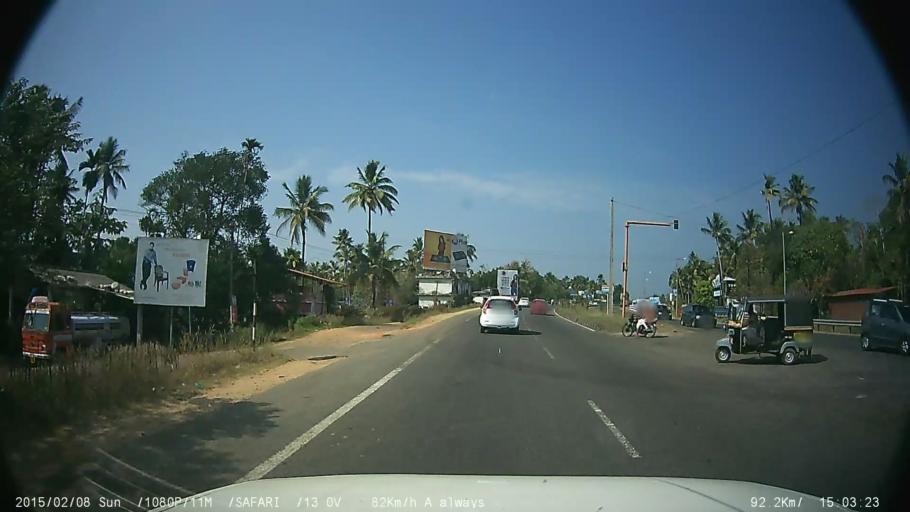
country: IN
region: Kerala
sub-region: Thrissur District
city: Kizhake Chalakudi
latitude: 10.3359
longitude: 76.3215
